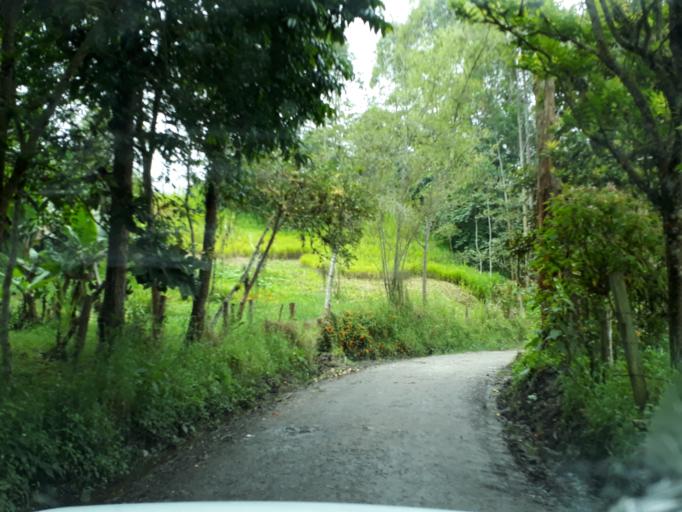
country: CO
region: Cundinamarca
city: Gacheta
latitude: 4.8490
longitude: -73.6477
